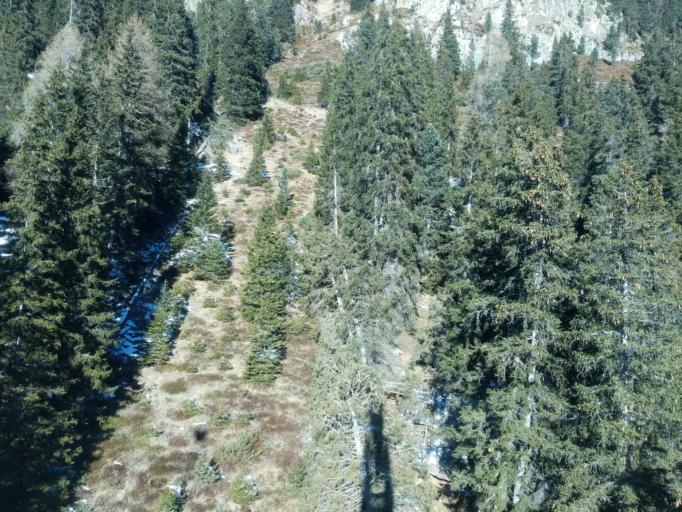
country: IT
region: Trentino-Alto Adige
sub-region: Provincia di Trento
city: Vigo di Fassa
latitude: 46.4315
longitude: 11.6663
